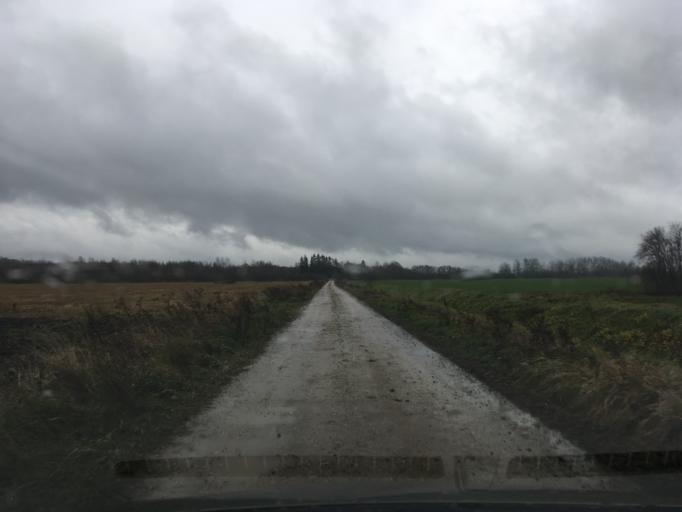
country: EE
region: Laeaene
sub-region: Lihula vald
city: Lihula
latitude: 58.7042
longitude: 23.8543
